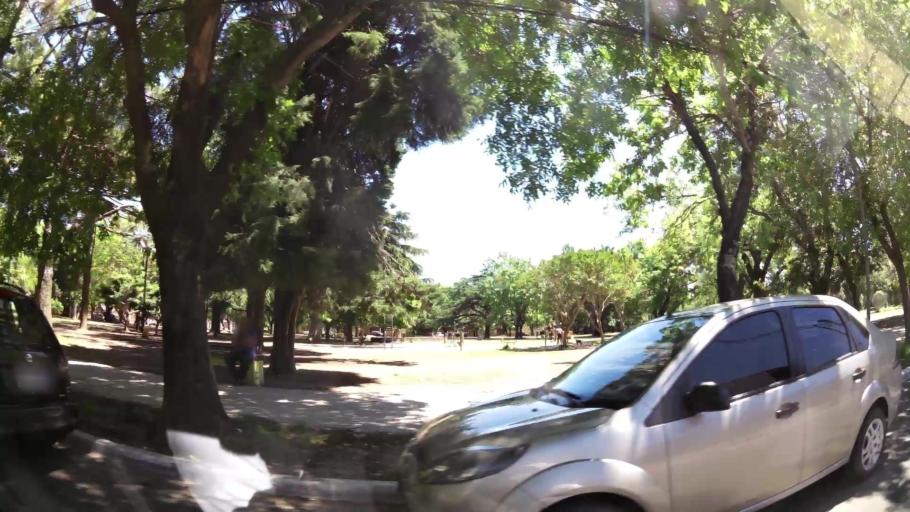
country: AR
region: Buenos Aires
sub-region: Partido de Quilmes
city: Quilmes
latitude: -34.7195
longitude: -58.2992
